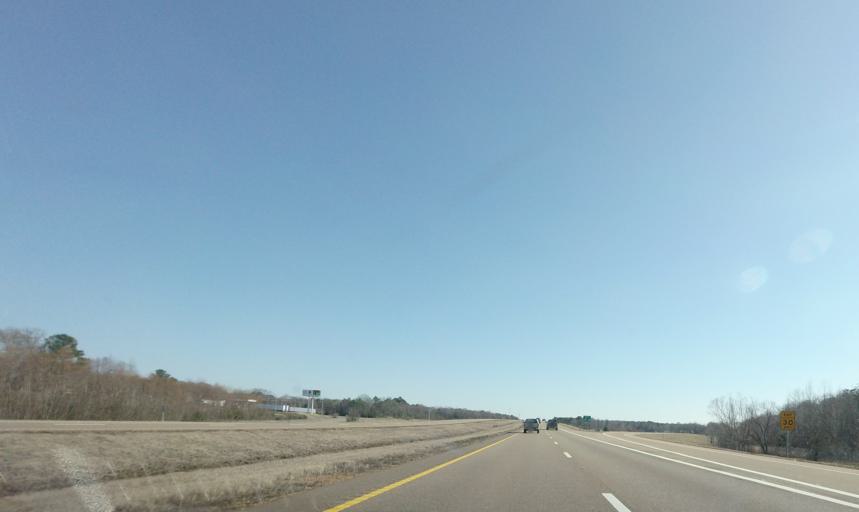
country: US
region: Mississippi
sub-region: Marshall County
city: Byhalia
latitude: 34.8273
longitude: -89.5702
